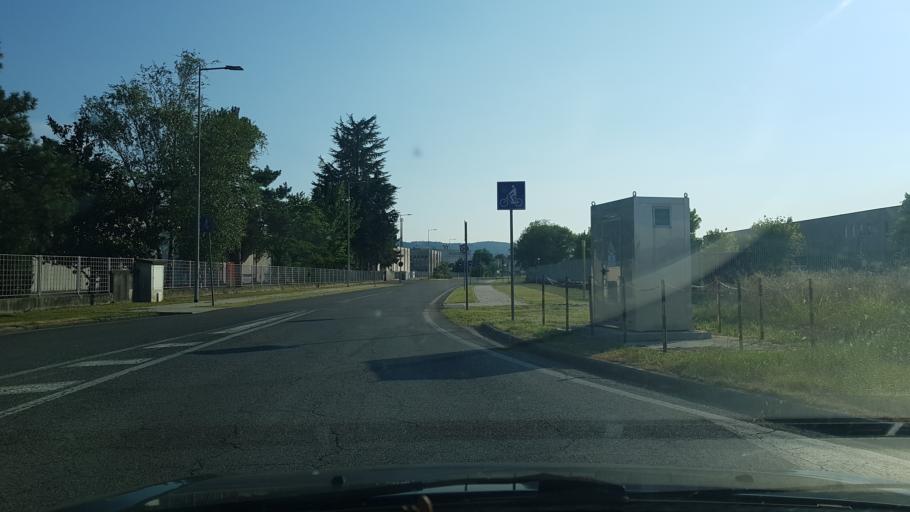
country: IT
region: Friuli Venezia Giulia
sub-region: Provincia di Gorizia
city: Savogna d'Isonzo
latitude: 45.9161
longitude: 13.5958
